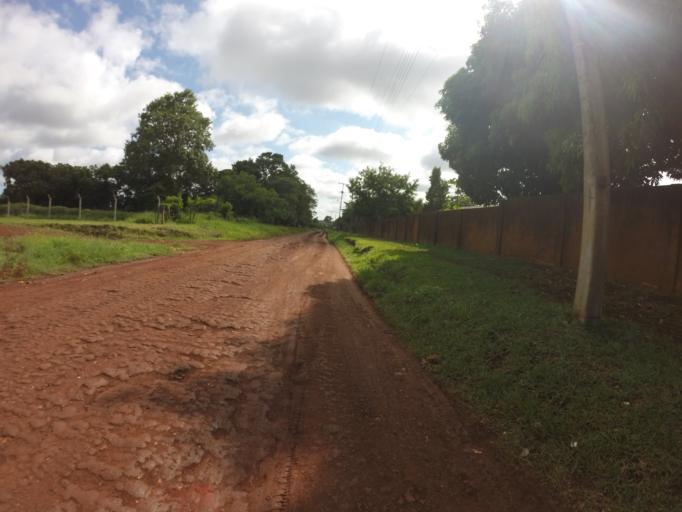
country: PY
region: Alto Parana
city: Ciudad del Este
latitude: -25.4086
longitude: -54.6585
